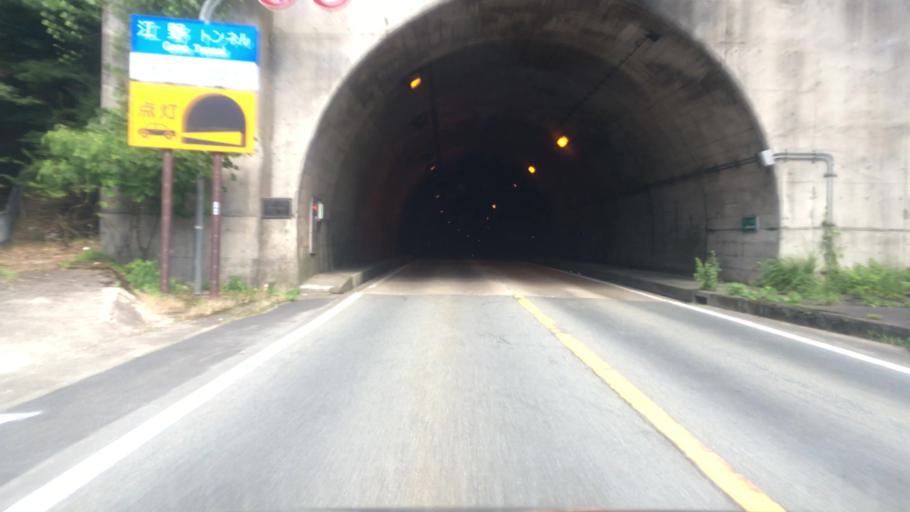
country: JP
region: Hyogo
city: Toyooka
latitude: 35.5782
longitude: 134.7499
